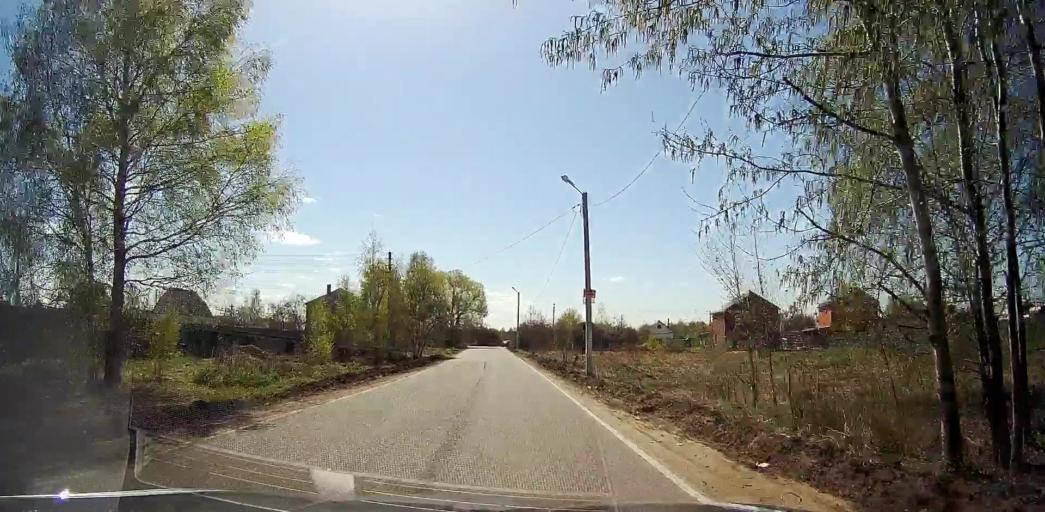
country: RU
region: Moskovskaya
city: Malyshevo
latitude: 55.4571
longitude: 38.3748
